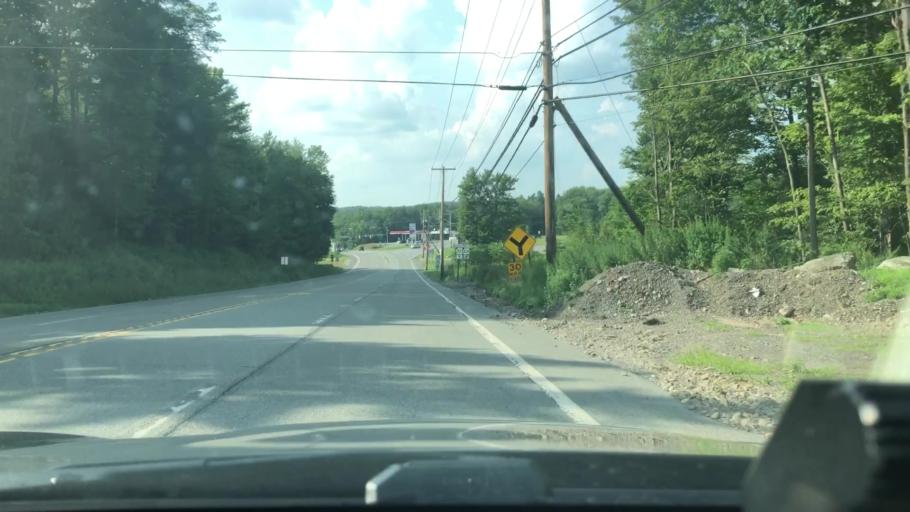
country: US
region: Pennsylvania
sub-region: Lackawanna County
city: Moscow
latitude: 41.2833
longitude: -75.5099
